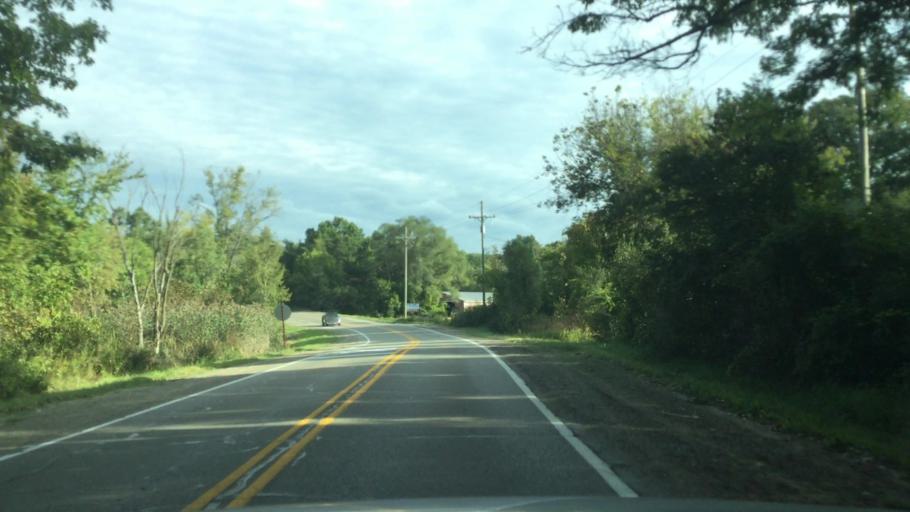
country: US
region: Michigan
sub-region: Livingston County
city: Brighton
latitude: 42.5165
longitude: -83.8557
